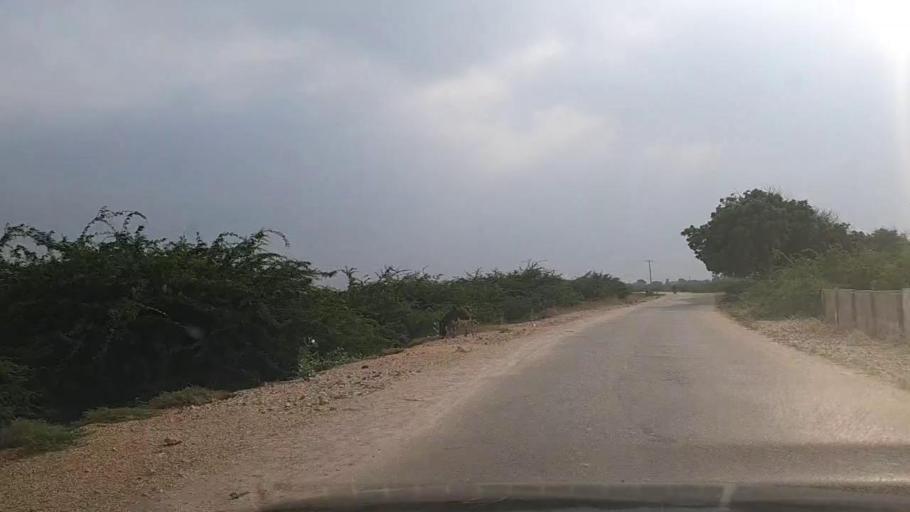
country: PK
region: Sindh
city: Thatta
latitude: 24.8534
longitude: 67.7782
